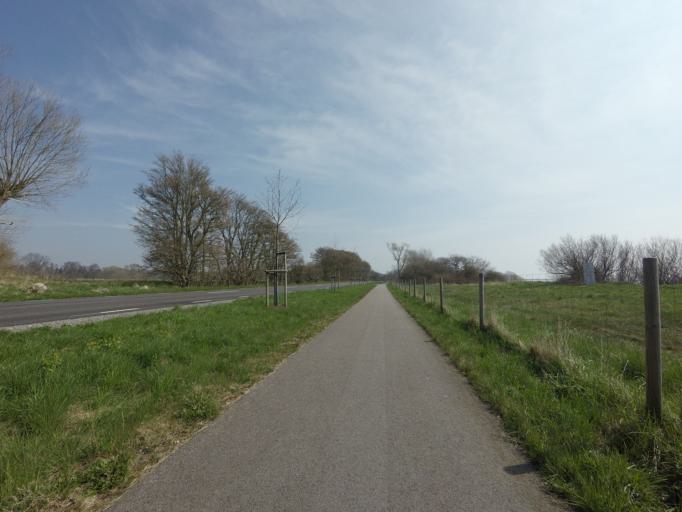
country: SE
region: Skane
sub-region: Skurups Kommun
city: Skivarp
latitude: 55.3876
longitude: 13.5323
